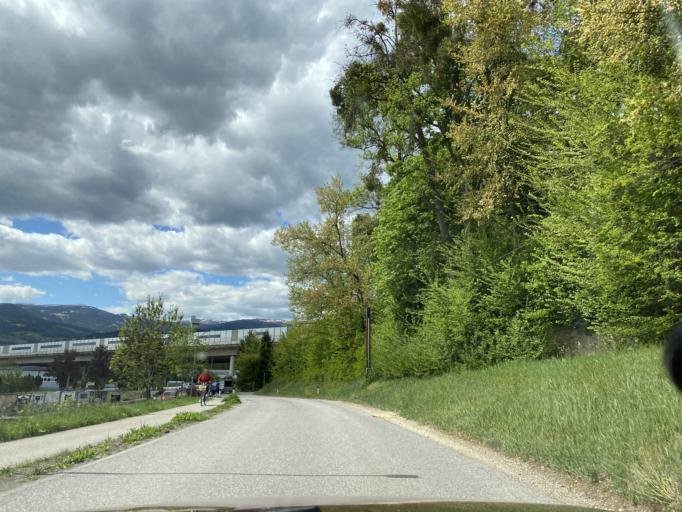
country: AT
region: Carinthia
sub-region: Politischer Bezirk Wolfsberg
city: Wolfsberg
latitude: 46.8439
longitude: 14.8334
